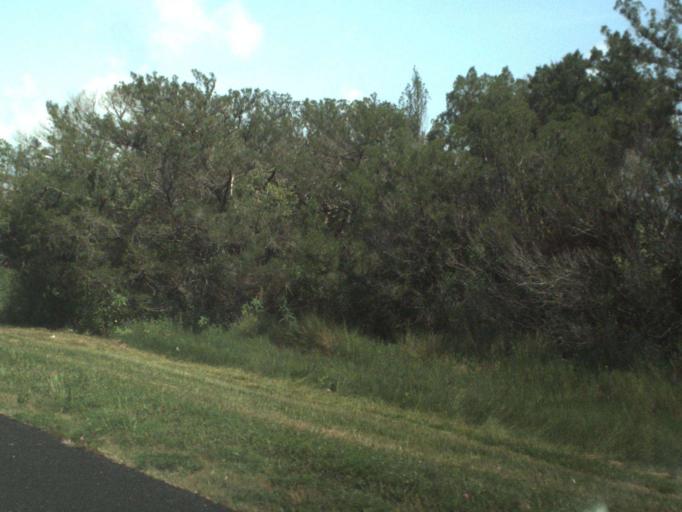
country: US
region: Florida
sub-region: Volusia County
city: Ormond Beach
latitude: 29.2972
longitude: -81.0813
